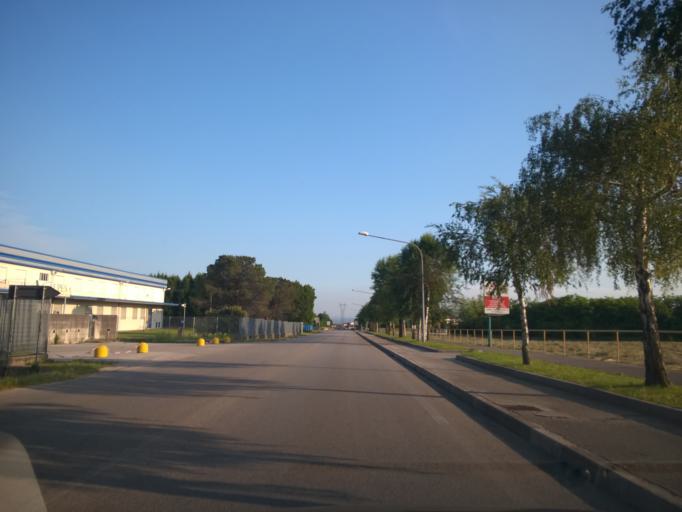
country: IT
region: Veneto
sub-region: Provincia di Vicenza
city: Carre
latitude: 45.7365
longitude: 11.4644
